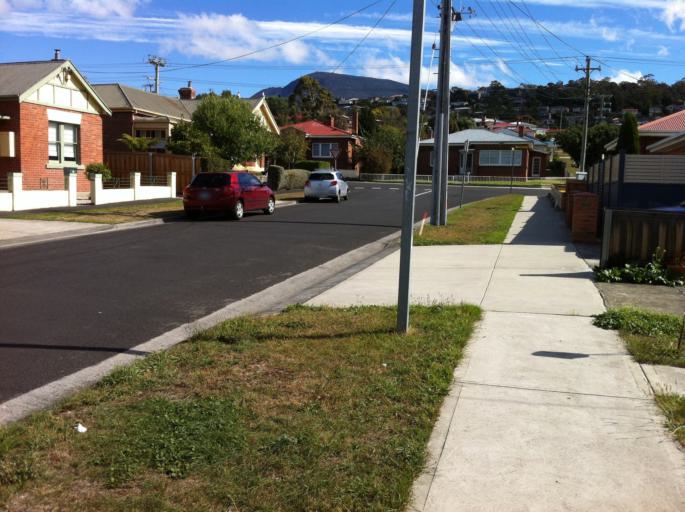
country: AU
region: Tasmania
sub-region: Glenorchy
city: Moonah
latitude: -42.8489
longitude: 147.2955
